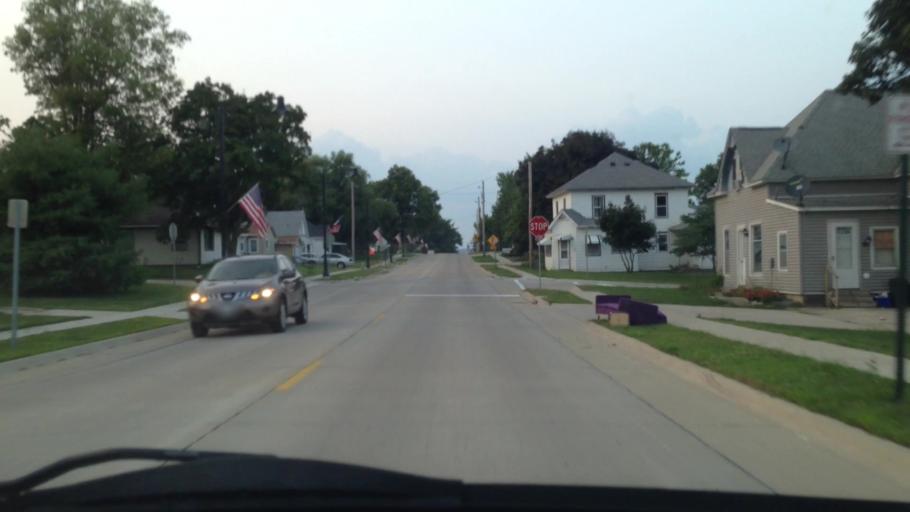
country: US
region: Iowa
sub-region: Benton County
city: Urbana
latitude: 42.2245
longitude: -91.8714
